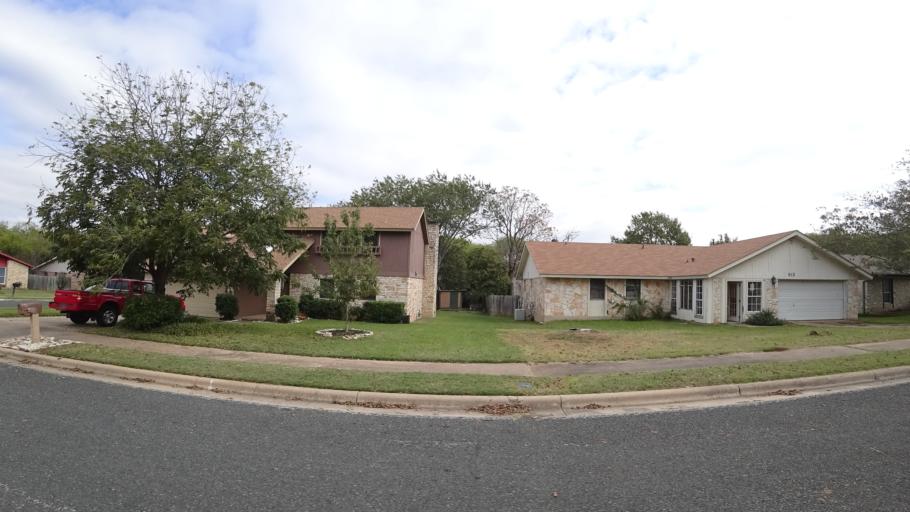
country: US
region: Texas
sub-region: Williamson County
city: Brushy Creek
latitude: 30.5180
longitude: -97.7369
